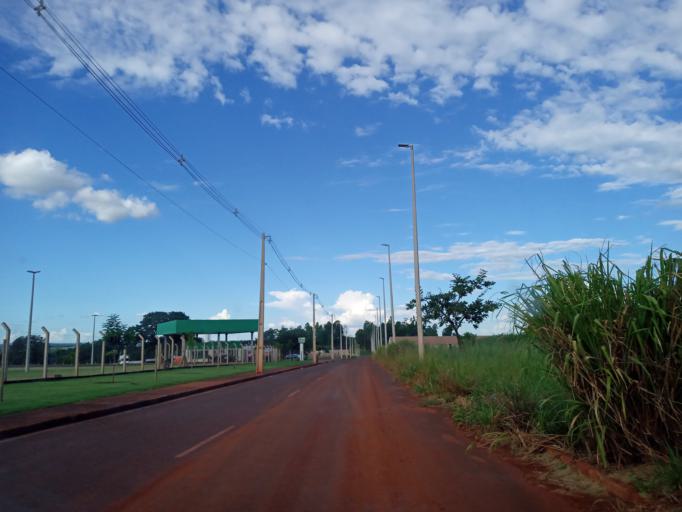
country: BR
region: Minas Gerais
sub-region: Ituiutaba
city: Ituiutaba
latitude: -18.9612
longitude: -49.4965
